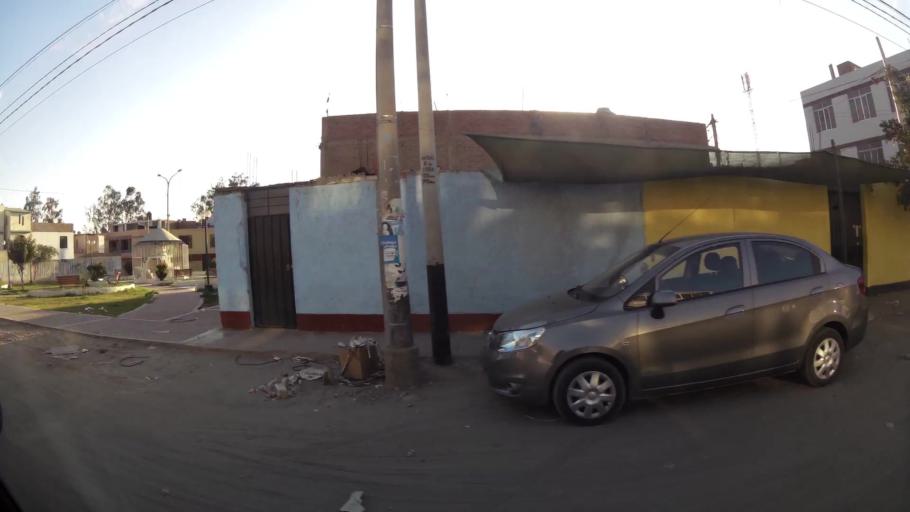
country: PE
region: Ica
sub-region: Provincia de Ica
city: Ica
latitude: -14.0582
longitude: -75.7342
